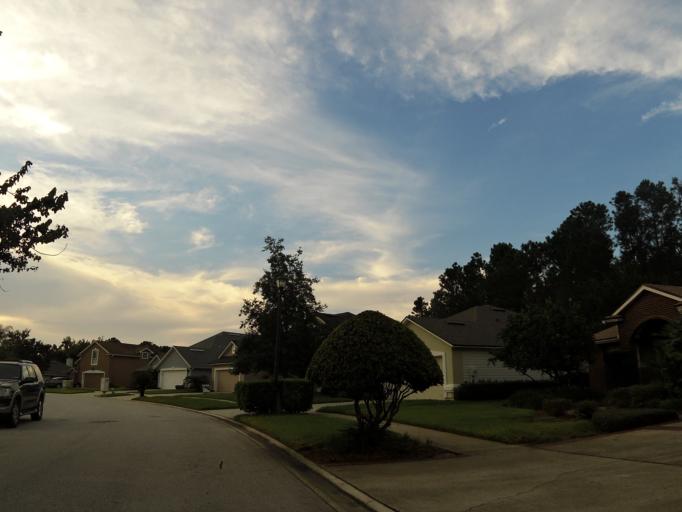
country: US
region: Florida
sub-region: Saint Johns County
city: Palm Valley
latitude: 30.2113
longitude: -81.5182
